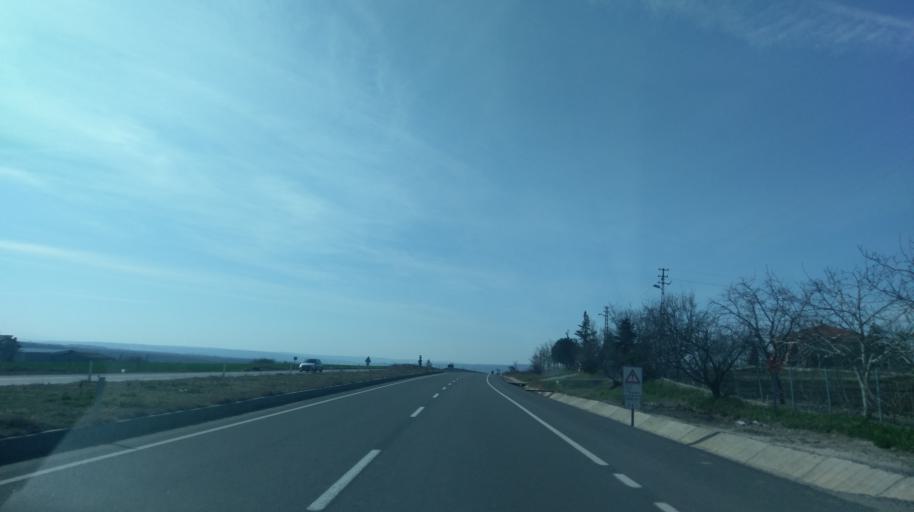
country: TR
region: Edirne
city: Hamidiye
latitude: 41.1507
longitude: 26.6621
